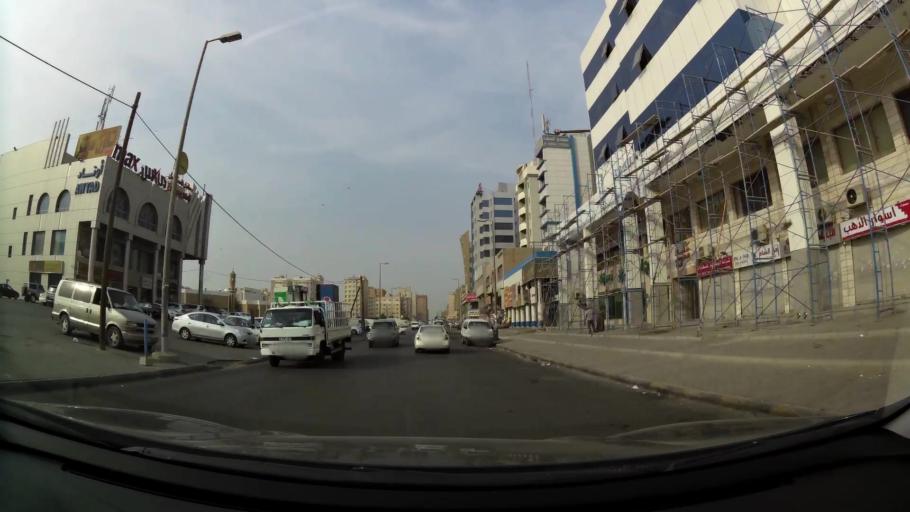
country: KW
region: Al Farwaniyah
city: Al Farwaniyah
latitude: 29.2896
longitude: 47.9746
